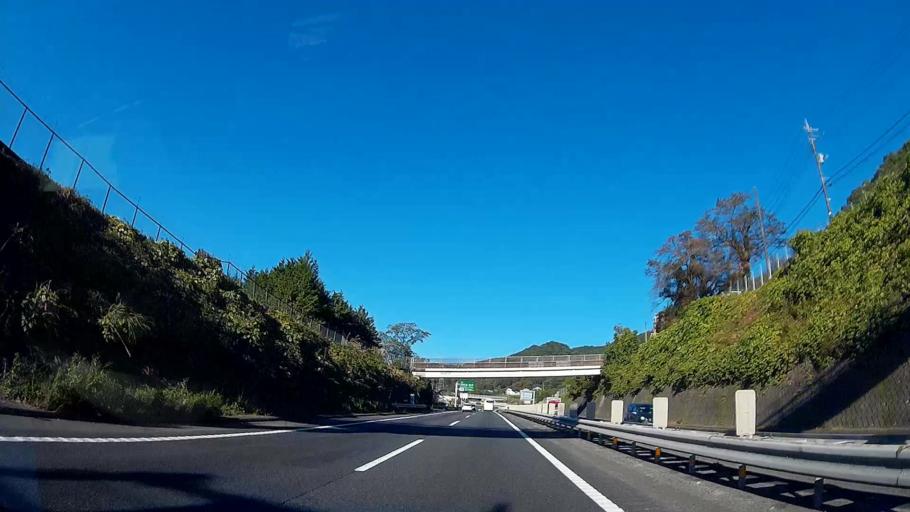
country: JP
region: Yamanashi
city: Uenohara
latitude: 35.6218
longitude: 139.1768
